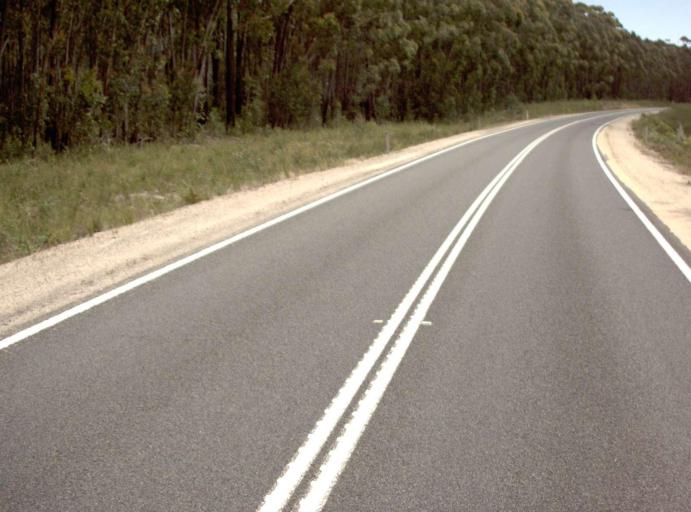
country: AU
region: New South Wales
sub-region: Bega Valley
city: Eden
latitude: -37.5330
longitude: 149.4848
